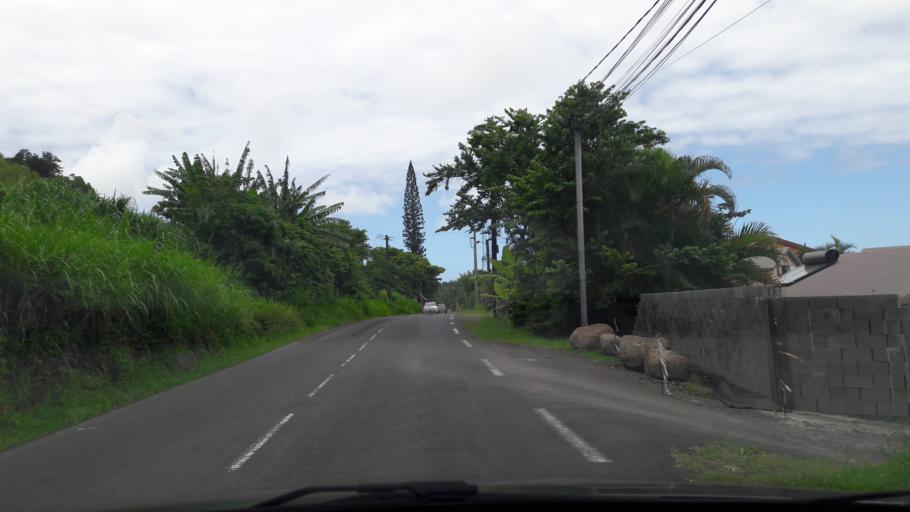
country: RE
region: Reunion
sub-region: Reunion
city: Saint-Andre
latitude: -20.9837
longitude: 55.6276
